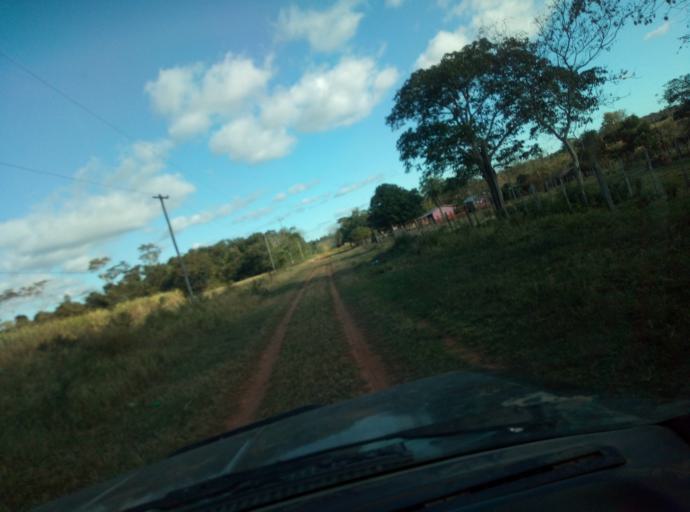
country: PY
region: Caaguazu
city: Doctor Cecilio Baez
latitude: -25.1678
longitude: -56.2728
